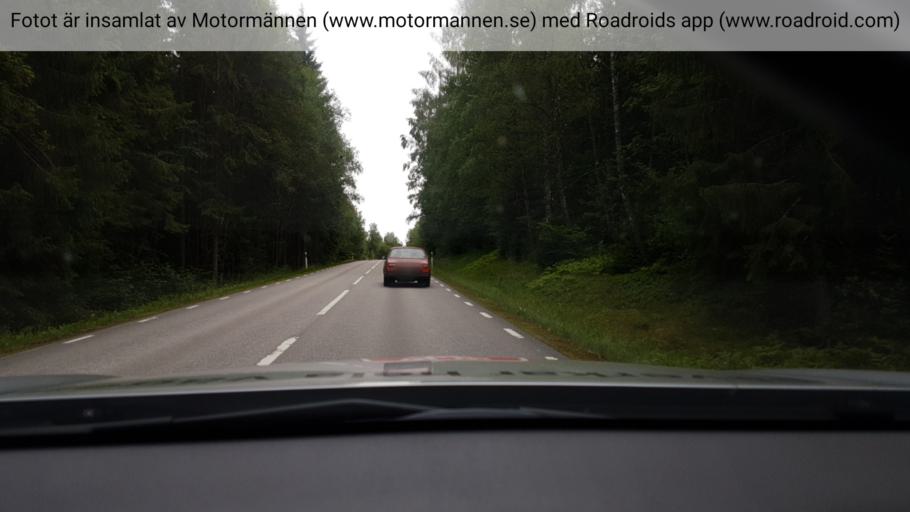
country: SE
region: Vaestra Goetaland
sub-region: Bengtsfors Kommun
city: Billingsfors
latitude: 58.9119
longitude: 12.2206
